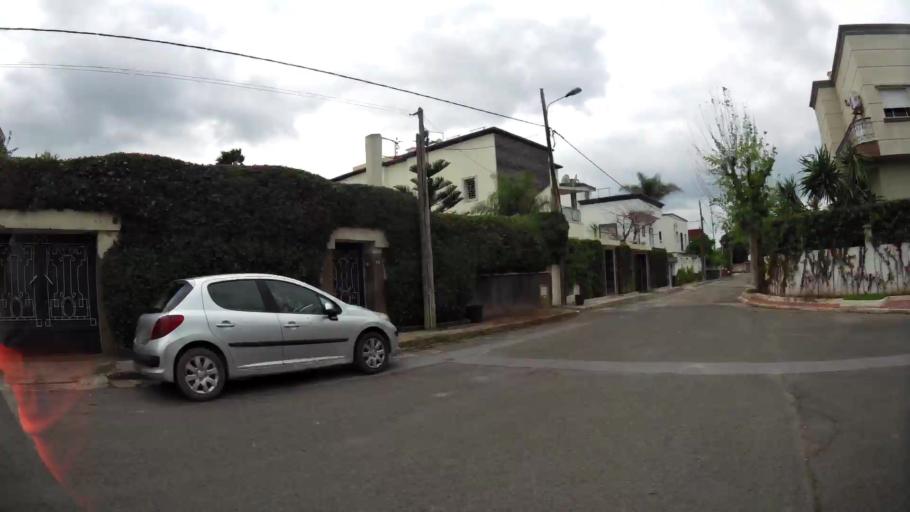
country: MA
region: Grand Casablanca
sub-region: Casablanca
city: Casablanca
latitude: 33.5544
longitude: -7.6218
